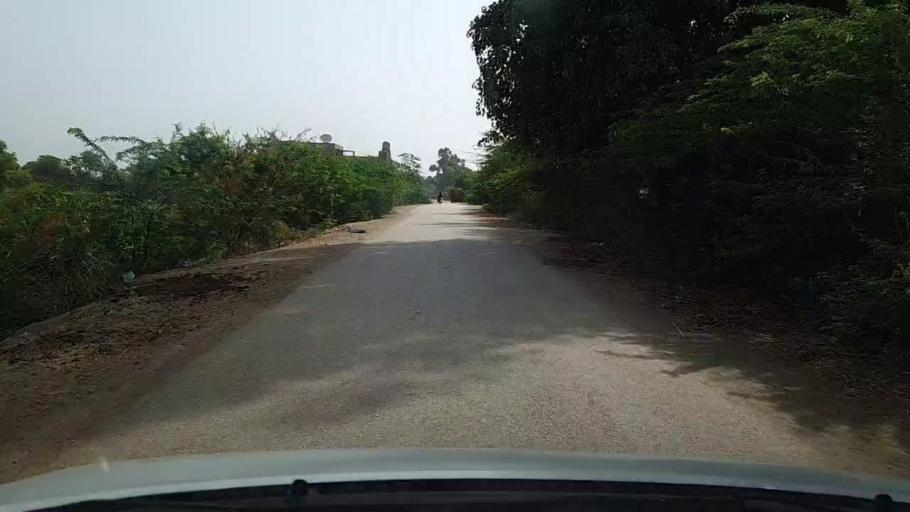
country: PK
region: Sindh
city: Mehar
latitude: 27.1265
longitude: 67.8633
